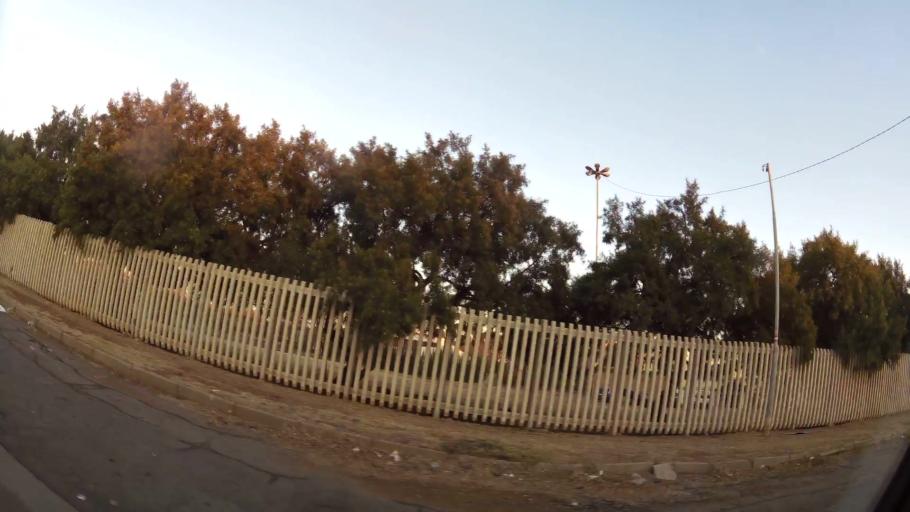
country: ZA
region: Gauteng
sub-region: Ekurhuleni Metropolitan Municipality
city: Germiston
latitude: -26.2705
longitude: 28.1580
